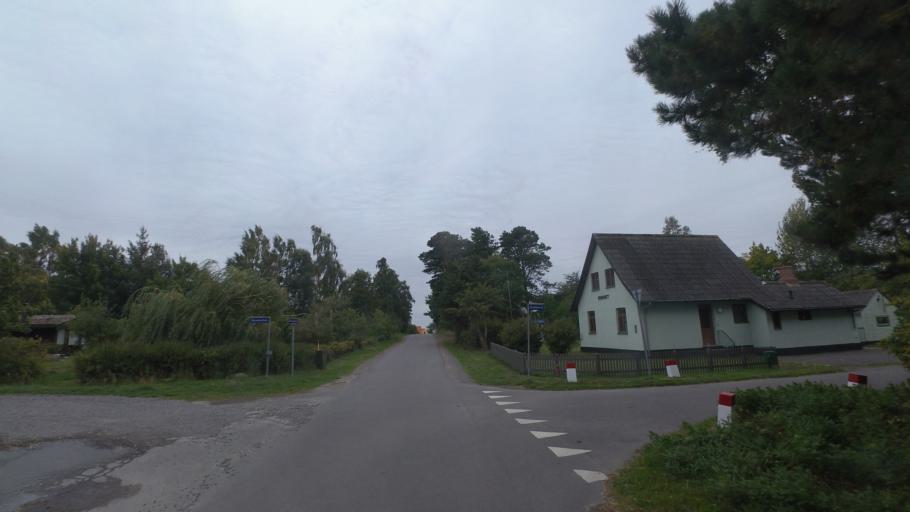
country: DK
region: Capital Region
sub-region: Bornholm Kommune
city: Akirkeby
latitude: 55.0029
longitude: 14.9919
